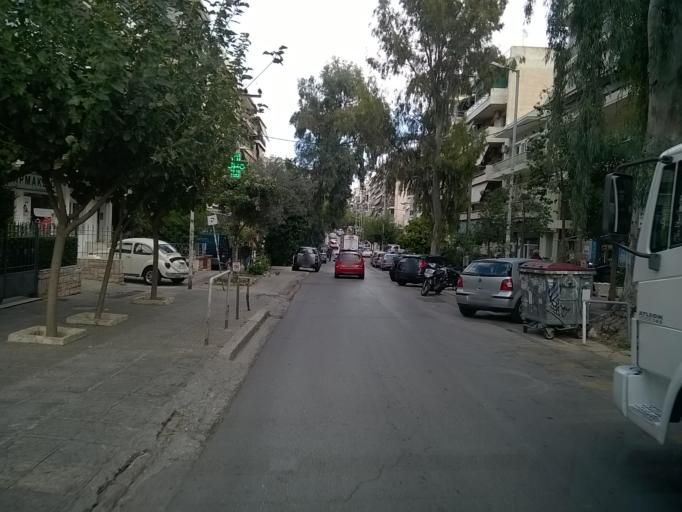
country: GR
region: Attica
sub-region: Nomarchia Athinas
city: Nea Smyrni
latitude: 37.9421
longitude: 23.7172
